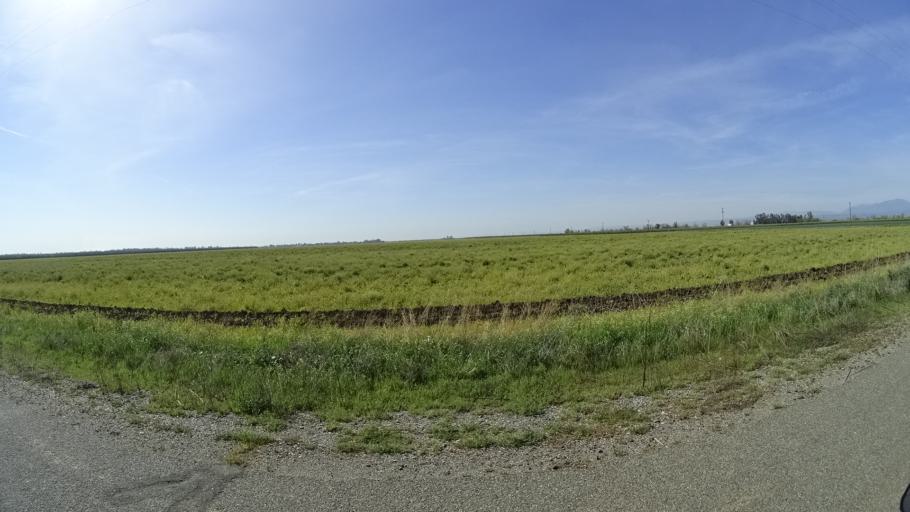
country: US
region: California
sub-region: Glenn County
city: Willows
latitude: 39.6114
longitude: -122.2298
